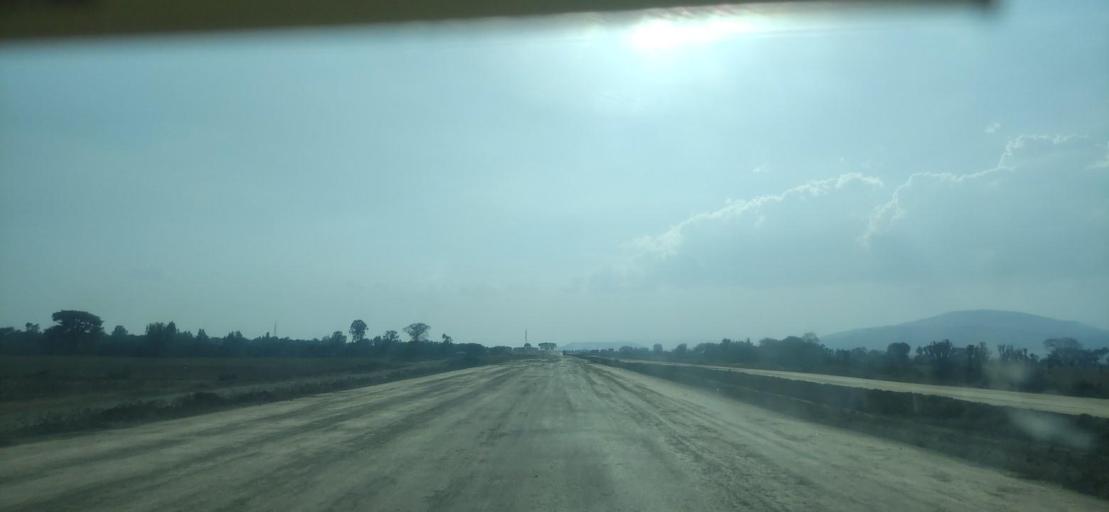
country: ET
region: Oromiya
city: Shashemene
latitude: 7.2000
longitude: 38.5357
